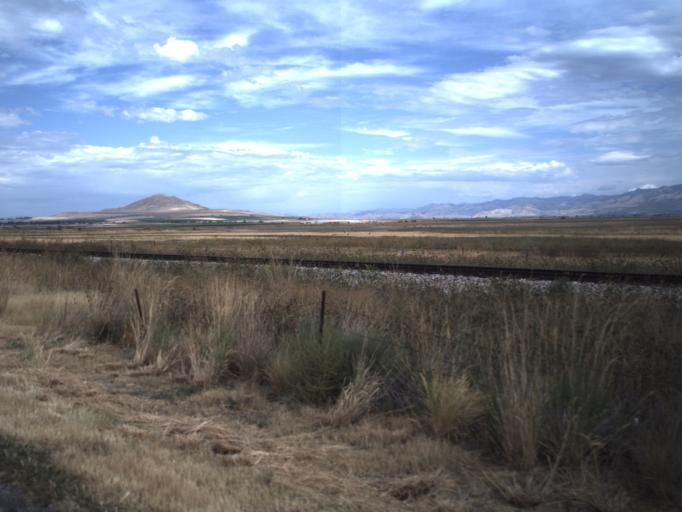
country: US
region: Utah
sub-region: Cache County
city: Benson
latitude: 41.7977
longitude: -111.9909
